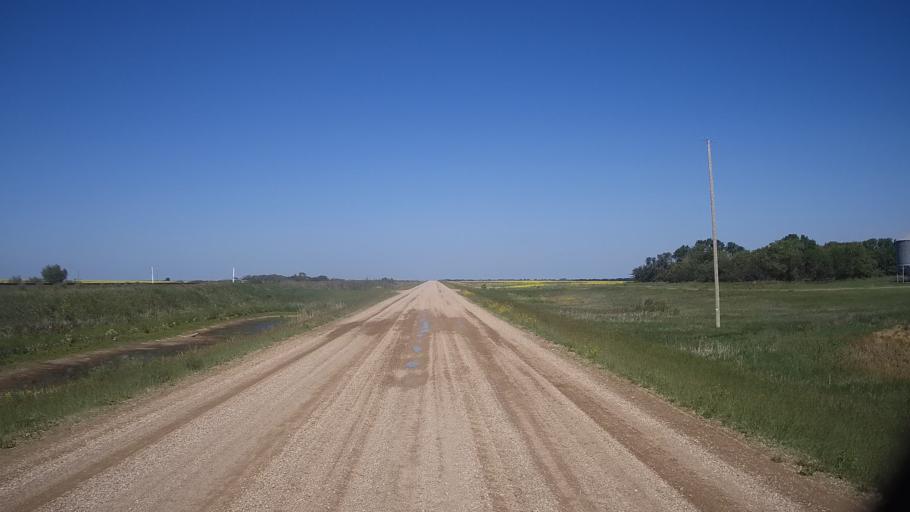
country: CA
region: Saskatchewan
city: Watrous
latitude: 51.8627
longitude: -105.9697
